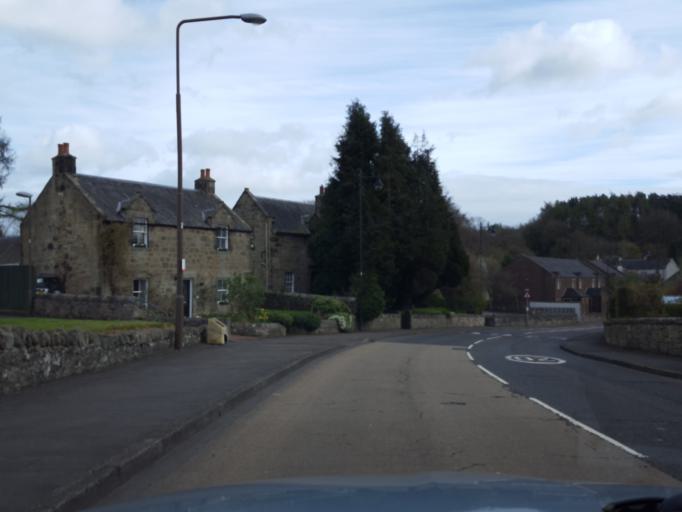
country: GB
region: Scotland
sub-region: West Lothian
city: Bathgate
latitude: 55.9349
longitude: -3.6554
